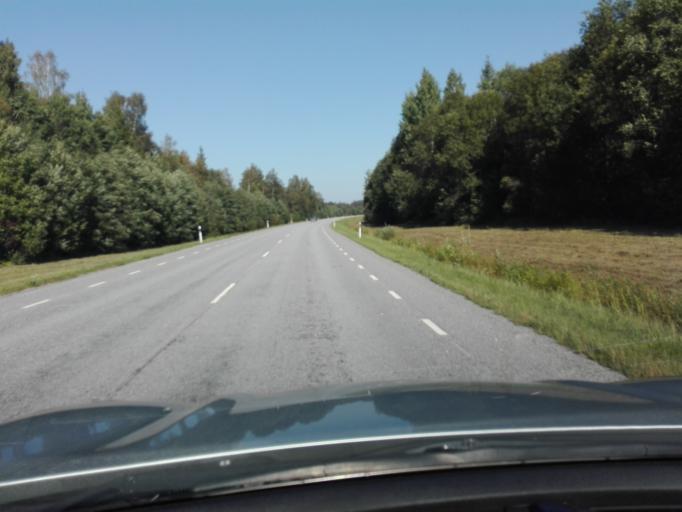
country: EE
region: Raplamaa
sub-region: Rapla vald
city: Rapla
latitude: 59.0105
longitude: 24.7714
